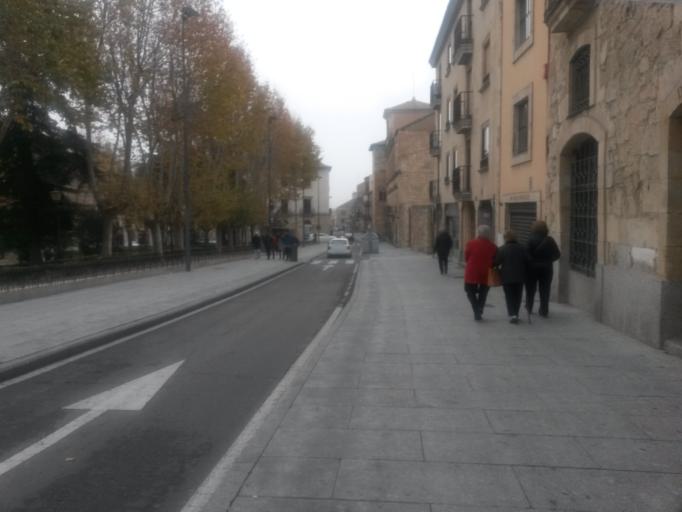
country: ES
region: Castille and Leon
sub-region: Provincia de Salamanca
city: Salamanca
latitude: 40.9629
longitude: -5.6642
